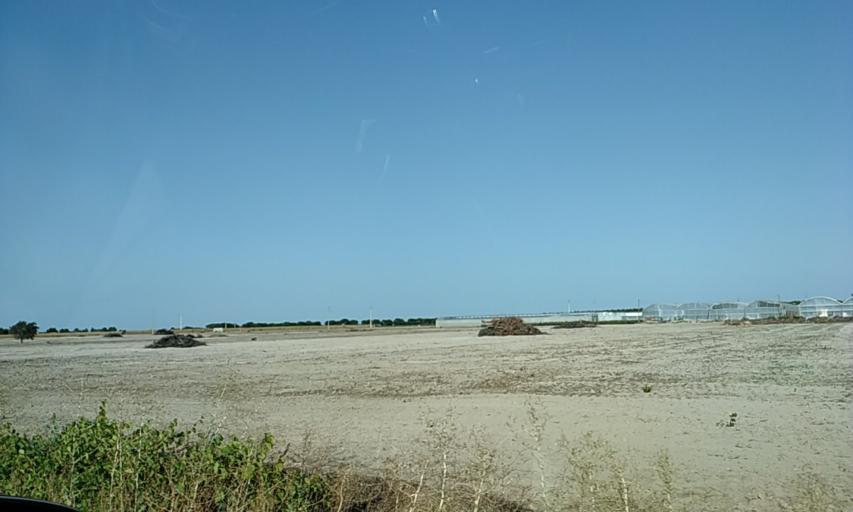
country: PT
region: Santarem
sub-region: Almeirim
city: Almeirim
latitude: 39.1672
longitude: -8.6205
